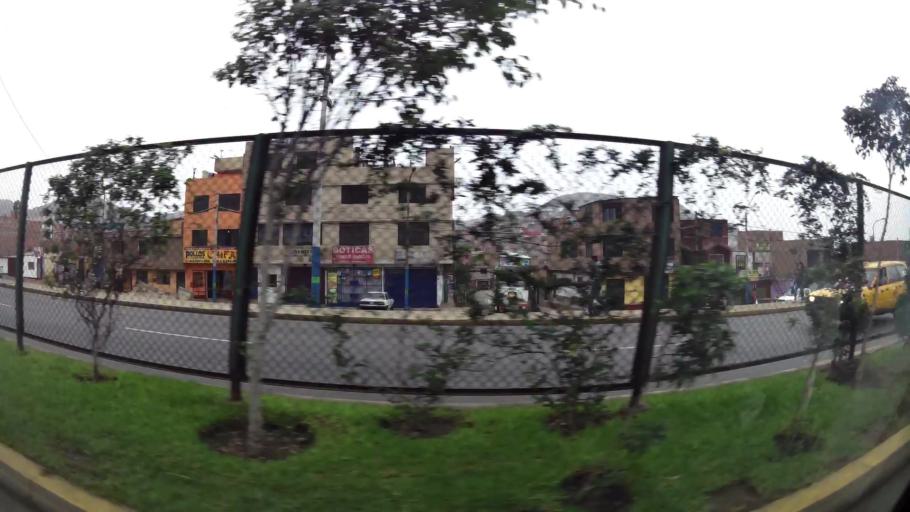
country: PE
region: Lima
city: Ventanilla
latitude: -11.8979
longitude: -77.1271
